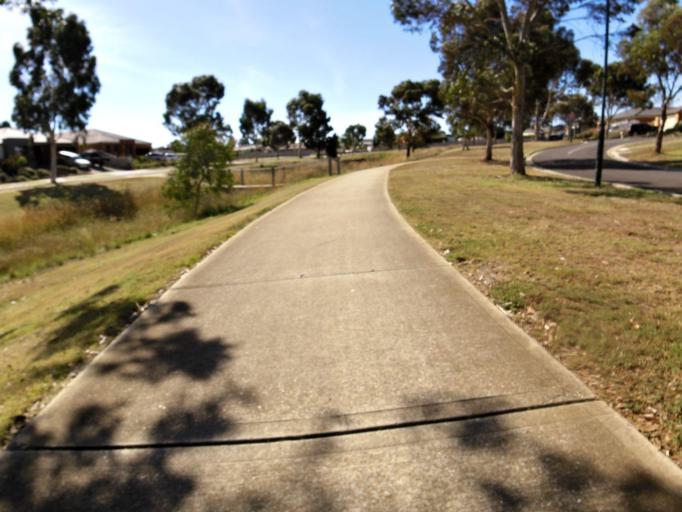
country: AU
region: Victoria
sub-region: Melton
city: Melton West
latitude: -37.6595
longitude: 144.5650
